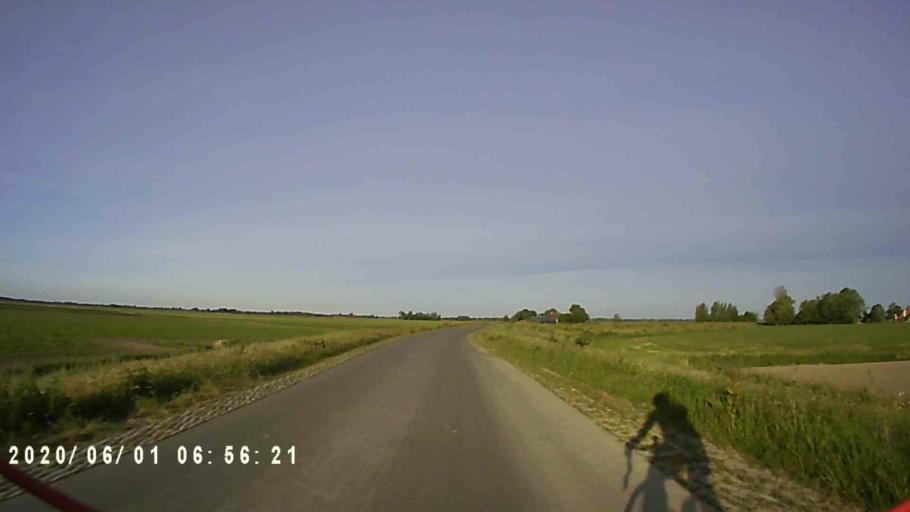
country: NL
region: Friesland
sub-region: Gemeente Kollumerland en Nieuwkruisland
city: Kollum
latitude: 53.3167
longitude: 6.1133
